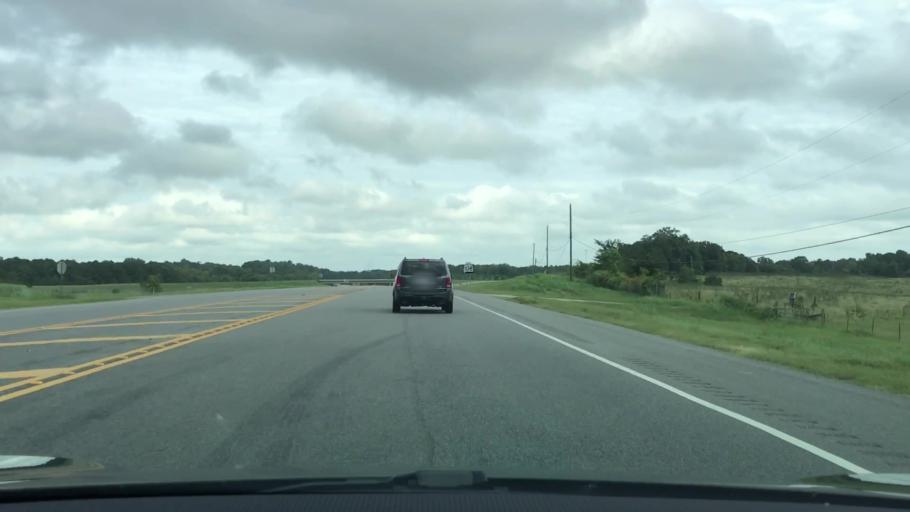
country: US
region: Alabama
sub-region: Montgomery County
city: Pike Road
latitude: 32.3337
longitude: -86.0583
